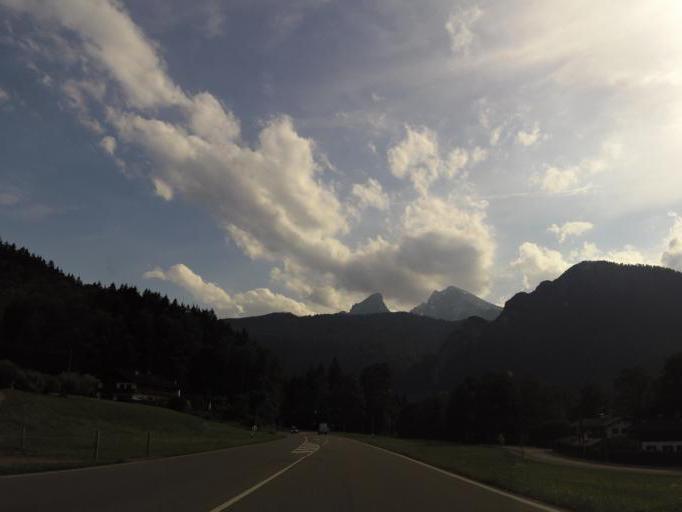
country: DE
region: Bavaria
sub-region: Upper Bavaria
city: Schoenau am Koenigssee
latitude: 47.6042
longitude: 12.9917
